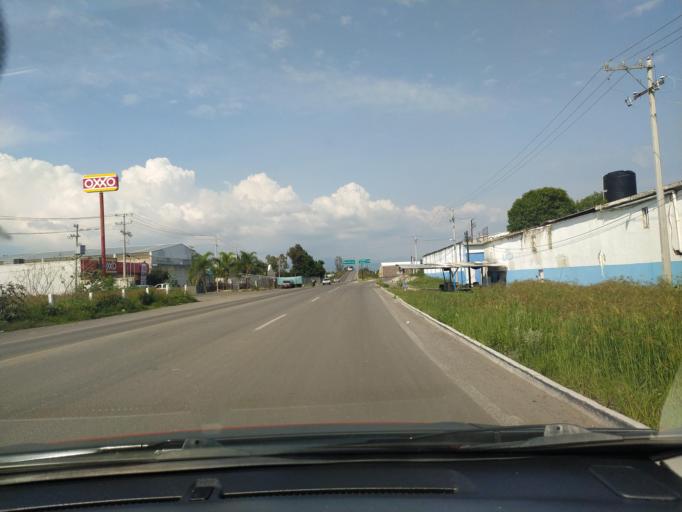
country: MX
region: Guanajuato
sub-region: Leon
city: Santa Ana
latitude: 21.0758
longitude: -101.7156
